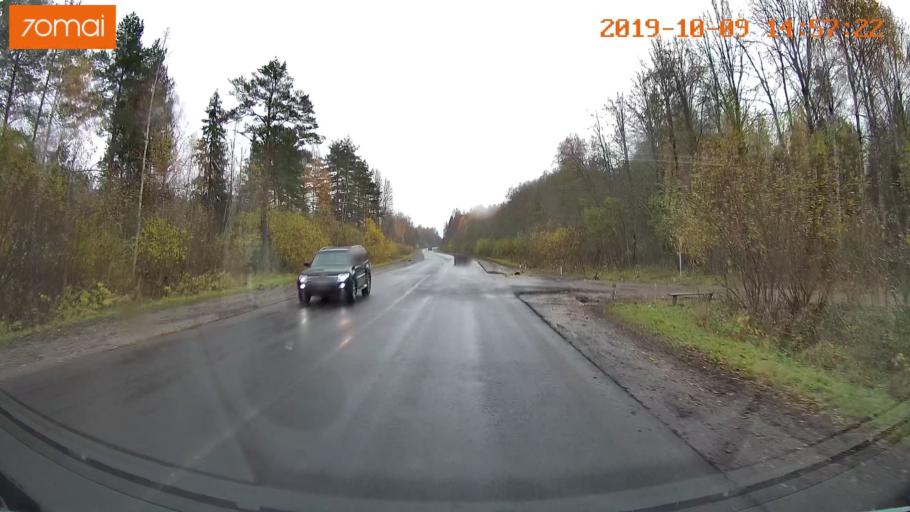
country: RU
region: Kostroma
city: Chistyye Bory
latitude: 58.3384
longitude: 41.6503
